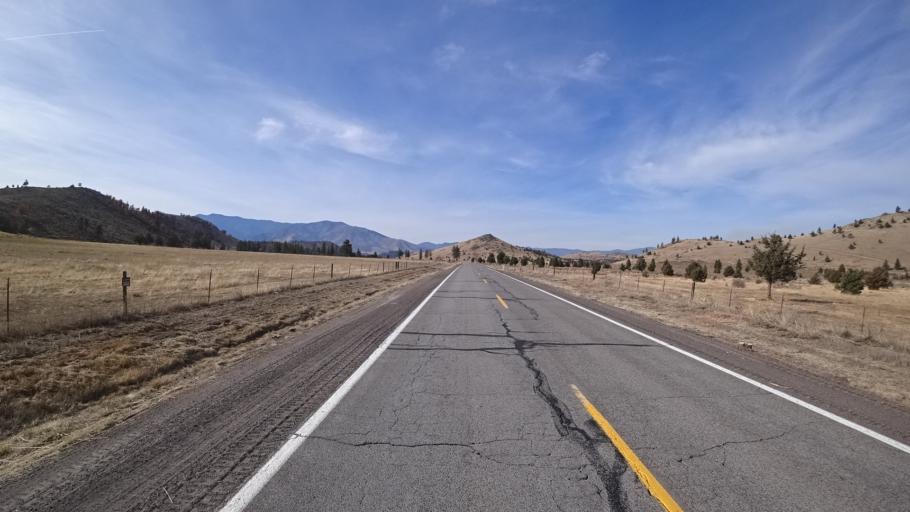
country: US
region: California
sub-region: Siskiyou County
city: Weed
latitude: 41.4940
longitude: -122.3887
